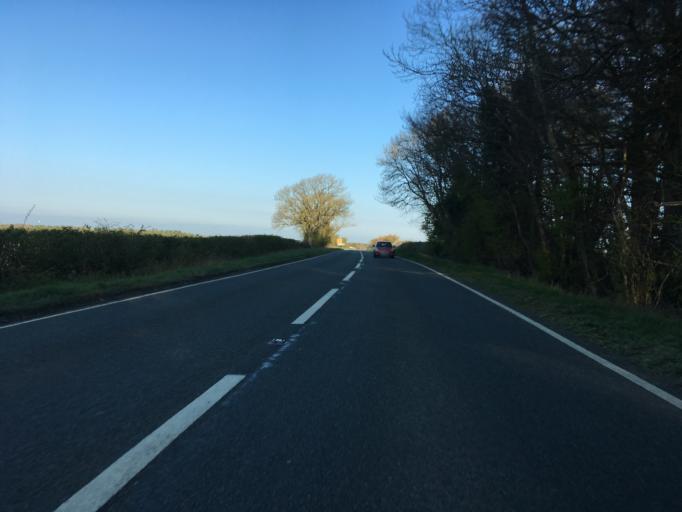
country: GB
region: England
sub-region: Gloucestershire
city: Bourton on the Water
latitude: 51.8088
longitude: -1.7183
